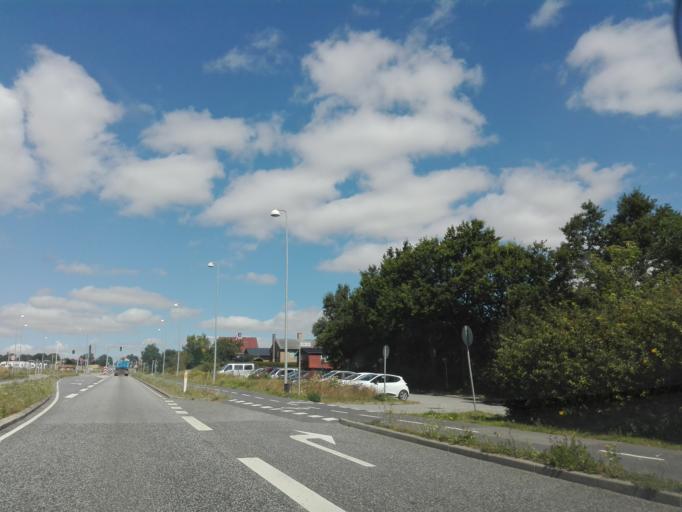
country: DK
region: Central Jutland
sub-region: Arhus Kommune
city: Trige
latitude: 56.2130
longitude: 10.1714
